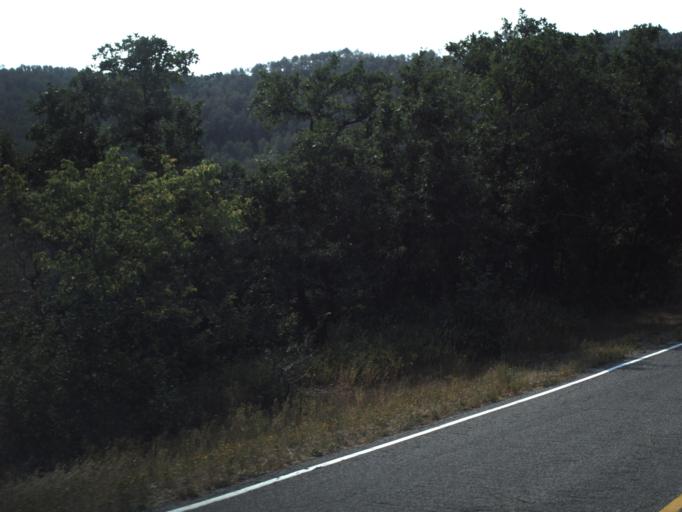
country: US
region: Utah
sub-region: Summit County
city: Summit Park
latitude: 40.8244
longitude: -111.6604
